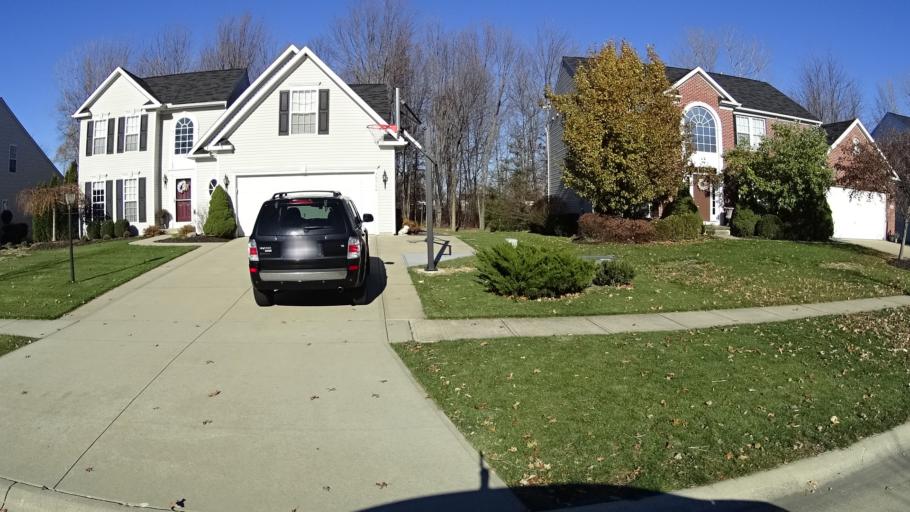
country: US
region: Ohio
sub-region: Lorain County
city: Avon
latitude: 41.4462
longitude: -82.0572
